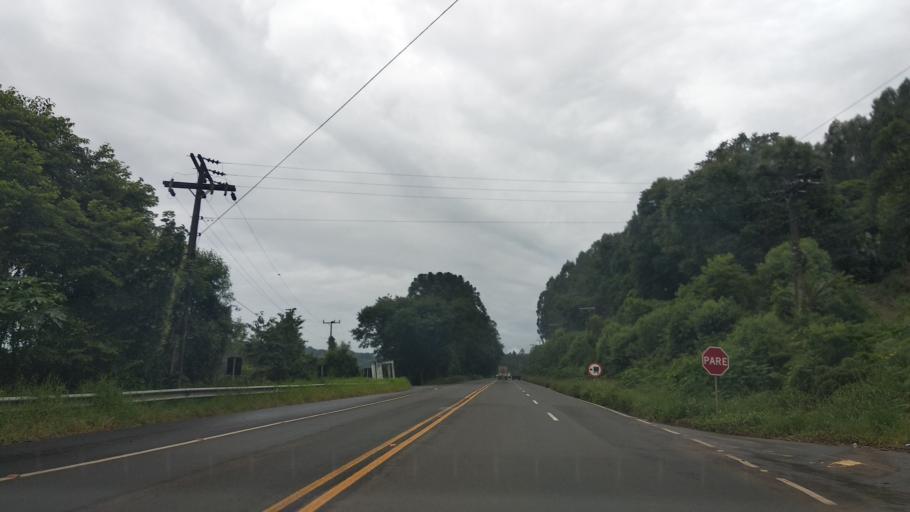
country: BR
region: Santa Catarina
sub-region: Videira
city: Videira
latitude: -27.0668
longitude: -51.2375
